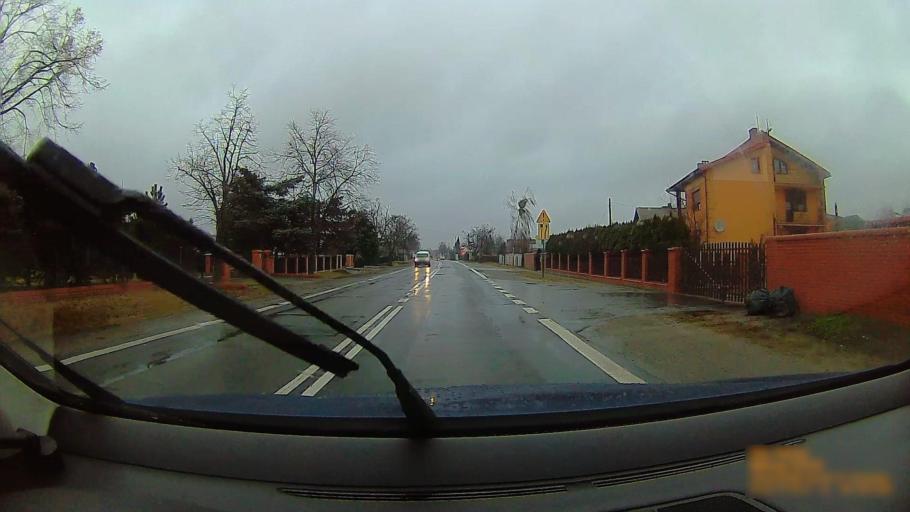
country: PL
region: Greater Poland Voivodeship
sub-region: Konin
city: Konin
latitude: 52.1866
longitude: 18.2673
